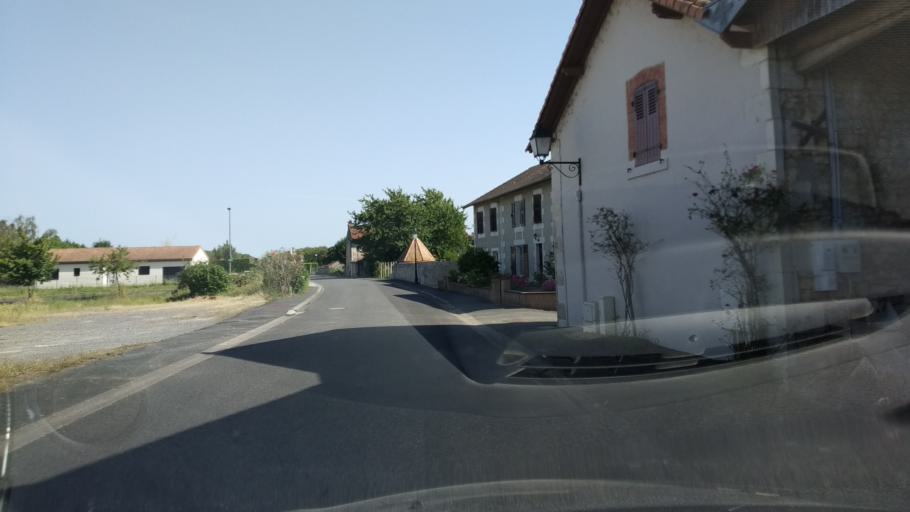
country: FR
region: Poitou-Charentes
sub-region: Departement de la Vienne
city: Lussac-les-Chateaux
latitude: 46.4425
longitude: 0.6676
